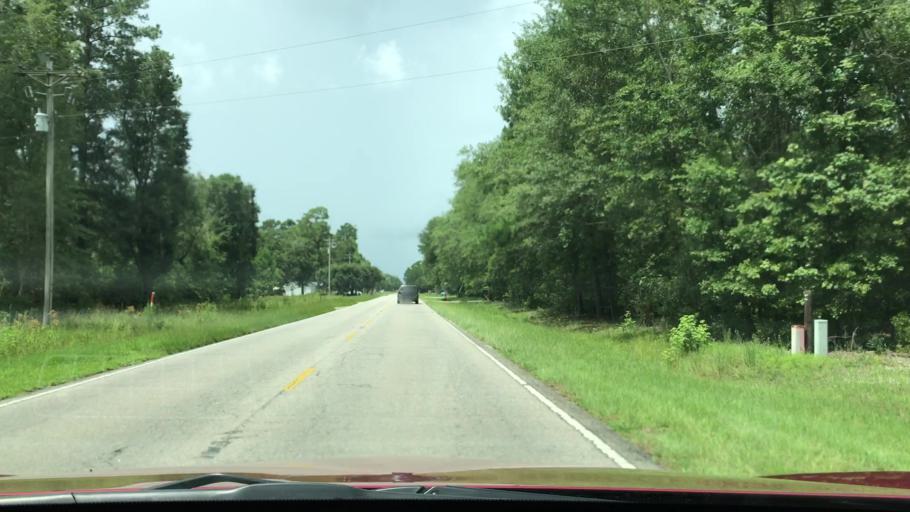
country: US
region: South Carolina
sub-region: Horry County
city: Red Hill
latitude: 33.8995
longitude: -78.9258
